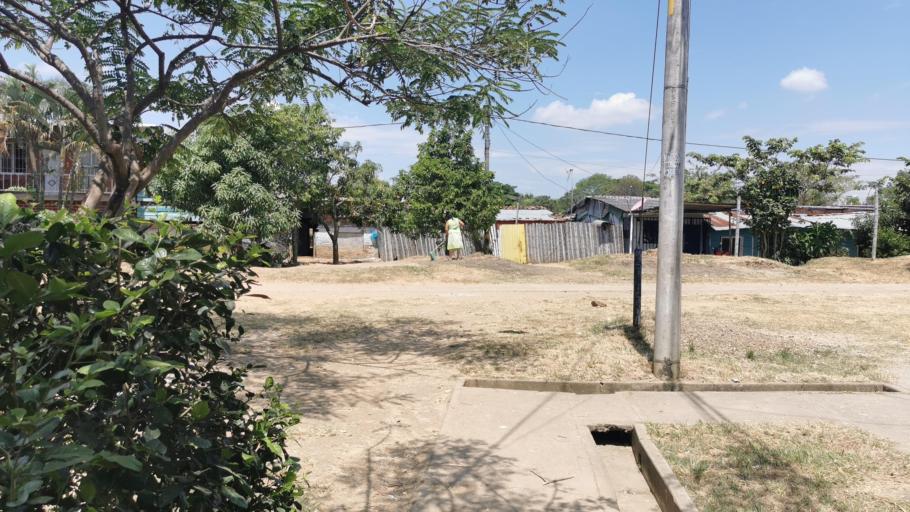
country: CO
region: Valle del Cauca
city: Jamundi
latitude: 3.2409
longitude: -76.5166
